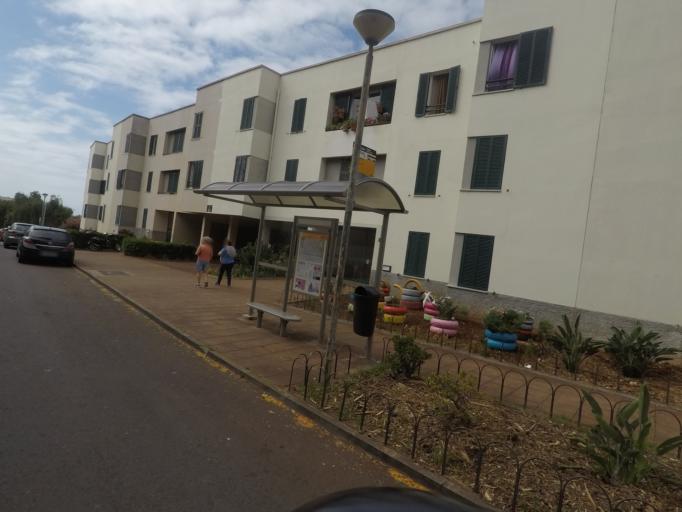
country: PT
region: Madeira
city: Camara de Lobos
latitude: 32.6472
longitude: -16.9358
